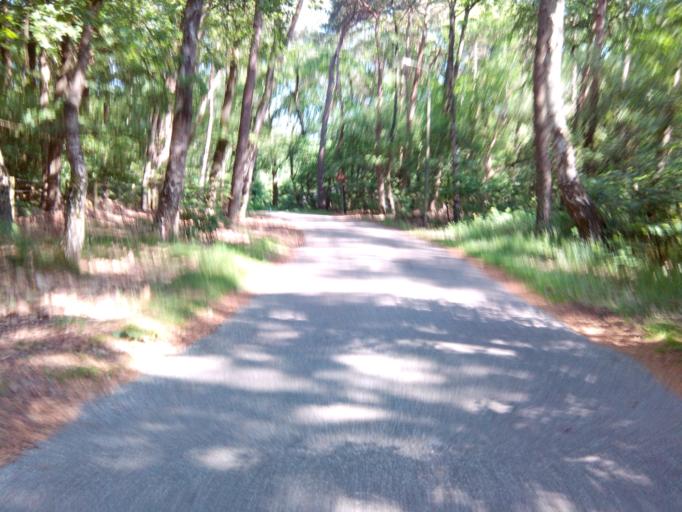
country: NL
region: Utrecht
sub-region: Gemeente Utrechtse Heuvelrug
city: Leersum
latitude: 52.0197
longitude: 5.4346
